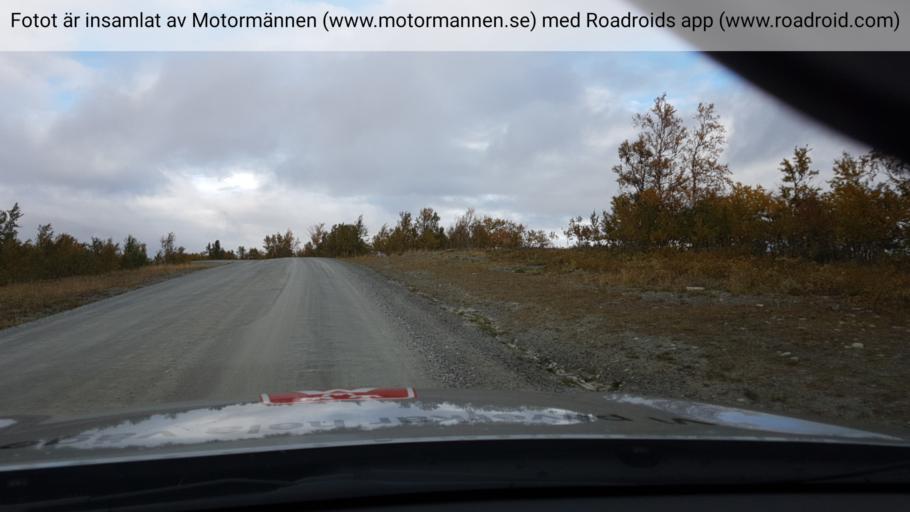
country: SE
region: Jaemtland
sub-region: Are Kommun
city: Are
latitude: 62.6473
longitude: 12.6620
